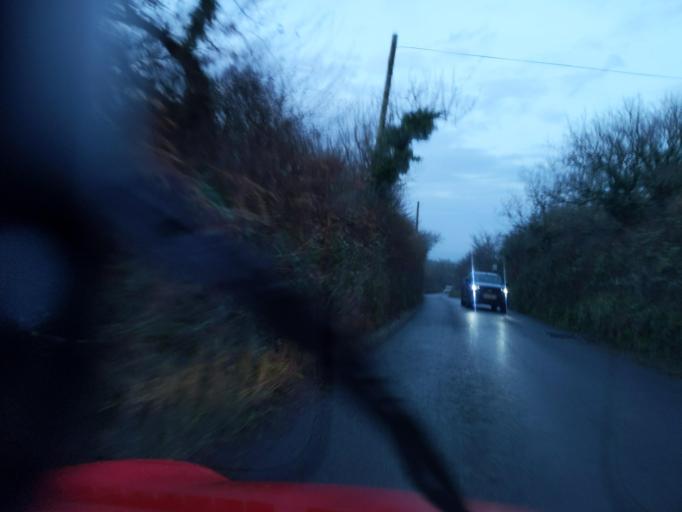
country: GB
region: England
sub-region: Plymouth
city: Plymstock
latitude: 50.3466
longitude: -4.0774
